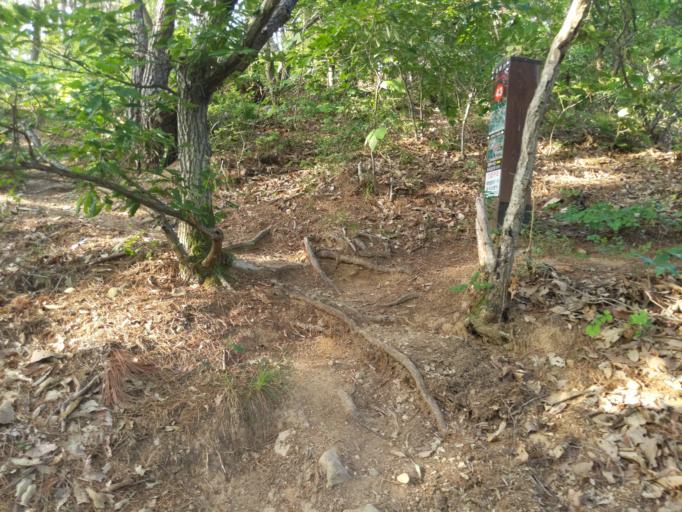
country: KR
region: Daegu
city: Hwawon
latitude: 35.7884
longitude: 128.5408
